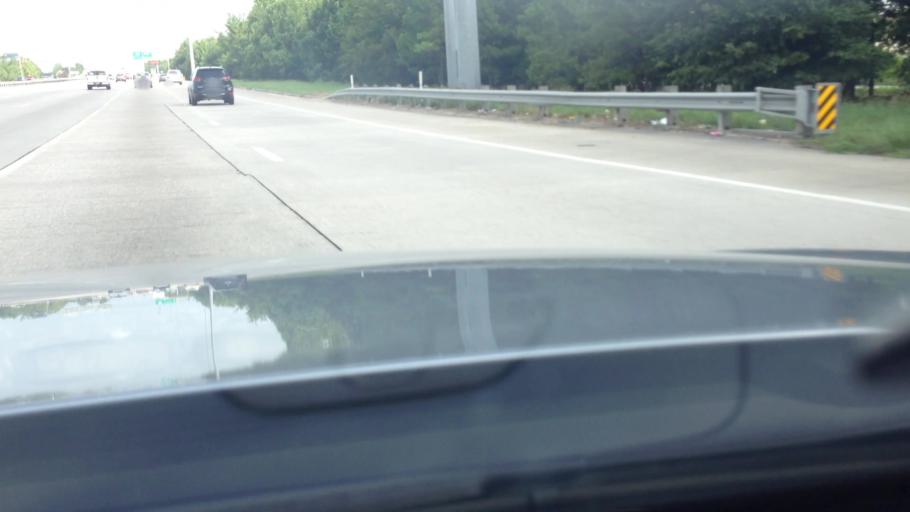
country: US
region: Texas
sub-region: Harris County
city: Hudson
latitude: 29.9475
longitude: -95.5296
